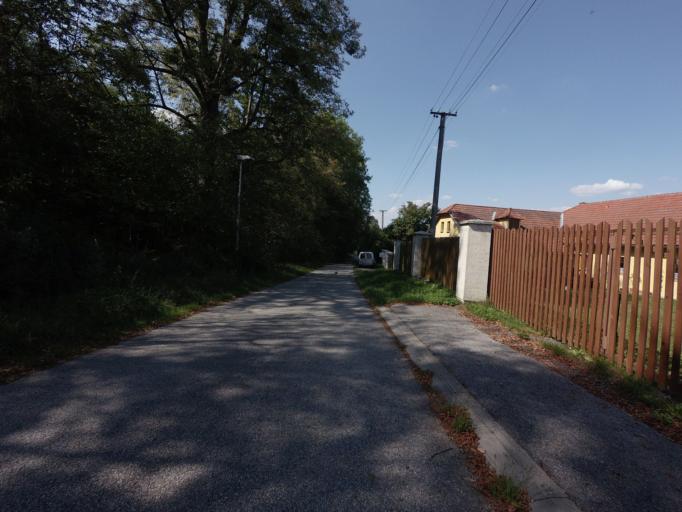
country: CZ
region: Jihocesky
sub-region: Okres Ceske Budejovice
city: Hluboka nad Vltavou
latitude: 49.1243
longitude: 14.4553
